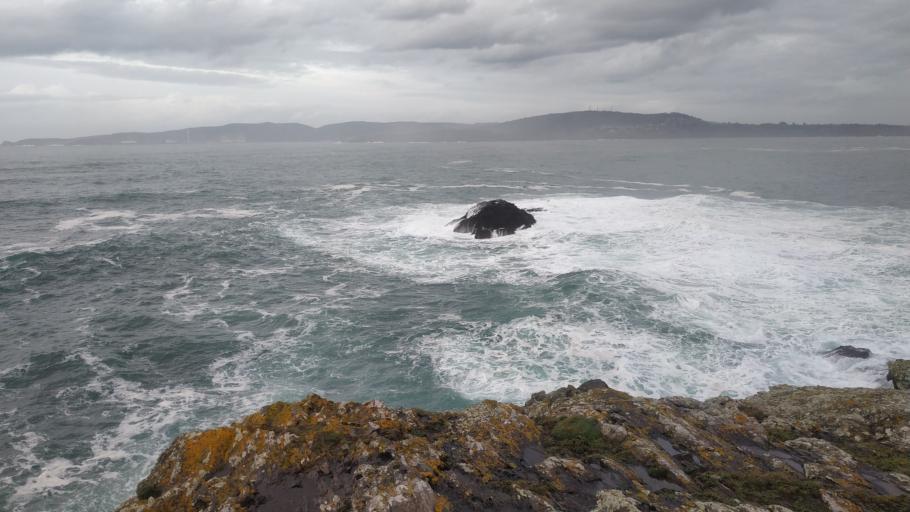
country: ES
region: Galicia
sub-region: Provincia da Coruna
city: Oleiros
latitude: 43.4027
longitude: -8.3284
